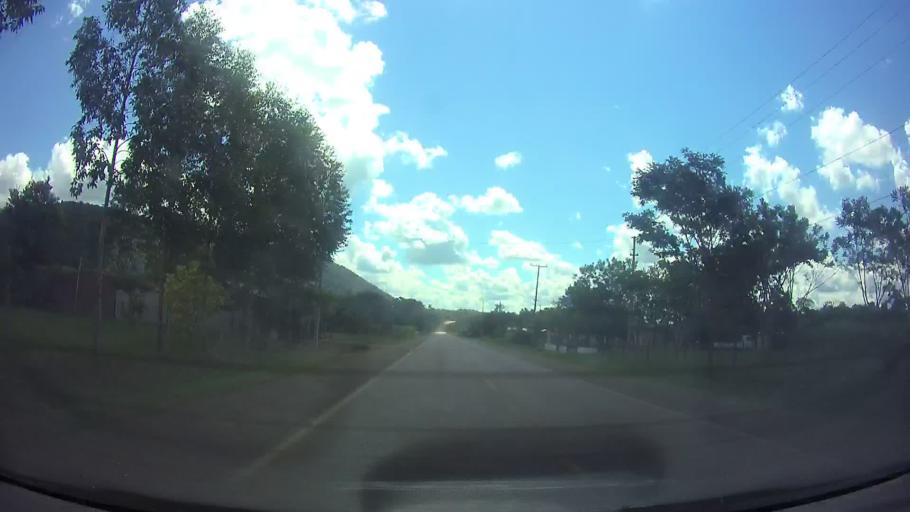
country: PY
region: Paraguari
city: La Colmena
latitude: -25.9183
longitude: -56.7286
